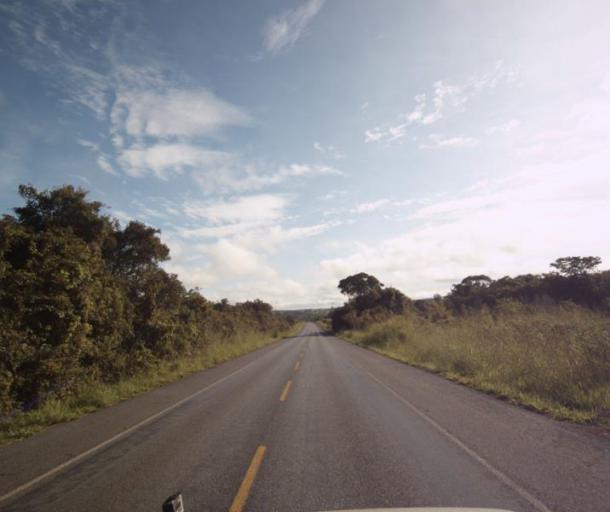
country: BR
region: Goias
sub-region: Padre Bernardo
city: Padre Bernardo
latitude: -15.5006
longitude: -48.6203
